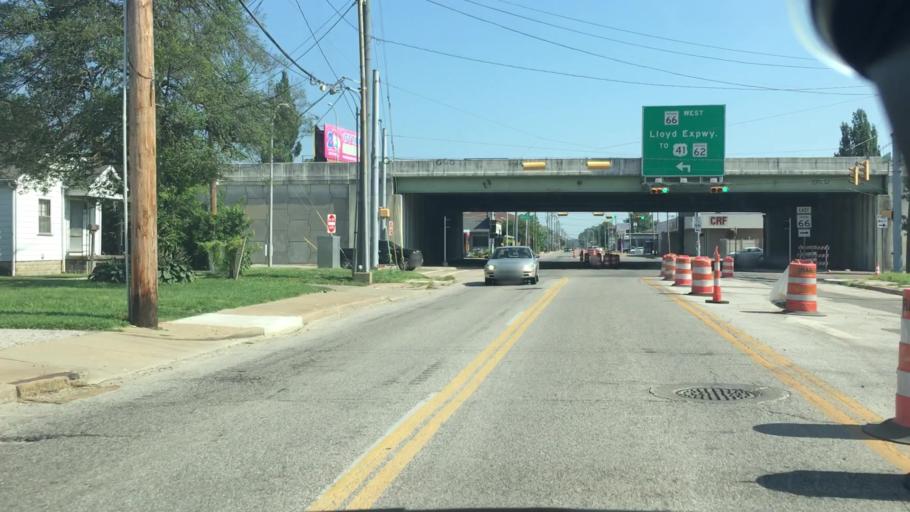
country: US
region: Indiana
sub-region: Vanderburgh County
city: Evansville
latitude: 37.9763
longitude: -87.5294
